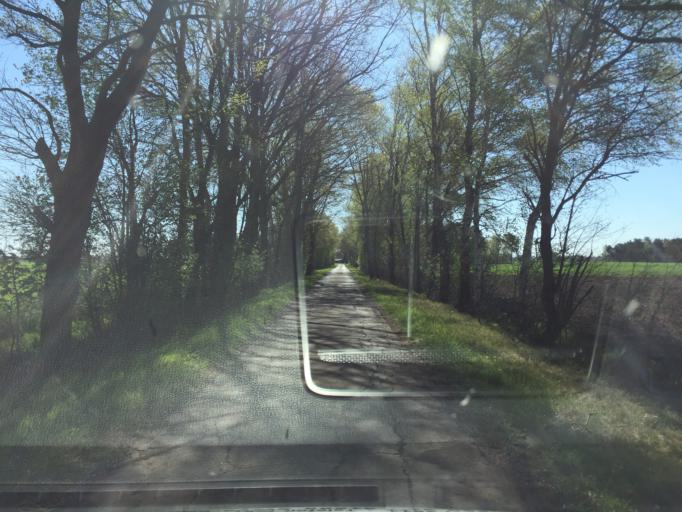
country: DE
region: Lower Saxony
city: Wehrbleck
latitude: 52.5707
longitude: 8.6849
